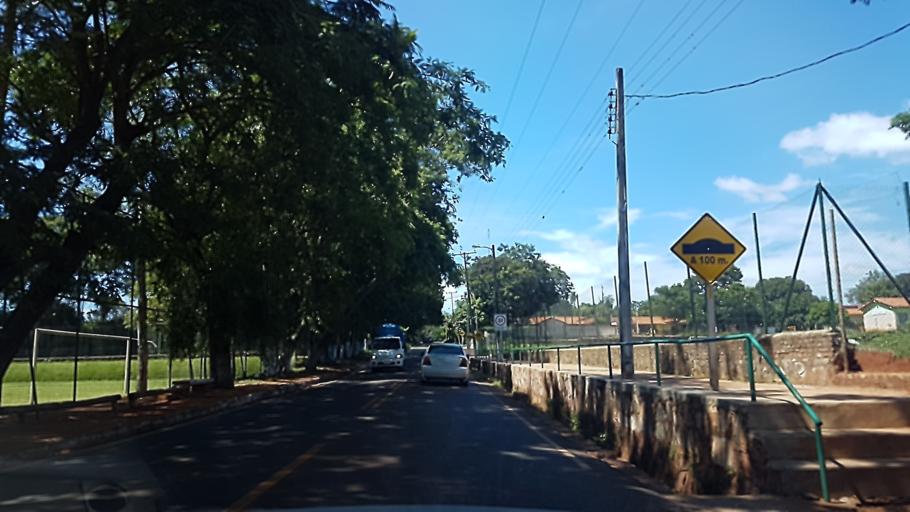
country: PY
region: Central
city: Capiata
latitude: -25.3274
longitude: -57.4409
